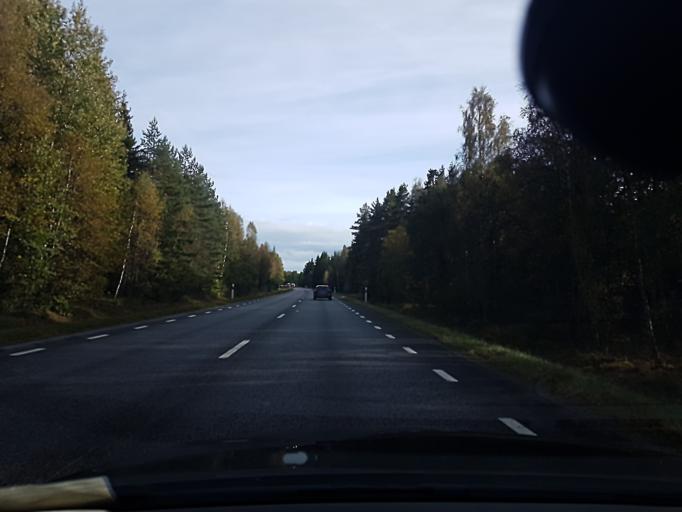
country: SE
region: Joenkoeping
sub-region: Varnamo Kommun
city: Varnamo
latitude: 57.1483
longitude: 14.0943
